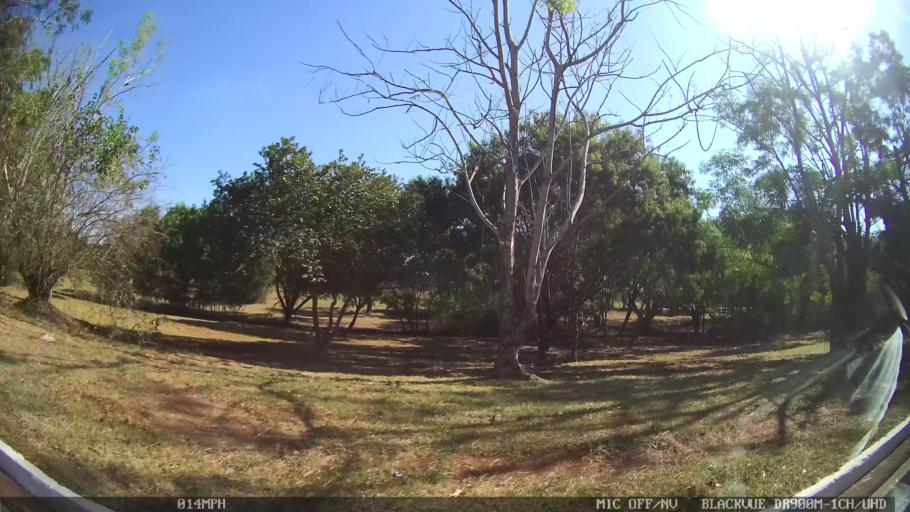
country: BR
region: Sao Paulo
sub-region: Ribeirao Preto
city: Ribeirao Preto
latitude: -21.2250
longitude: -47.7677
